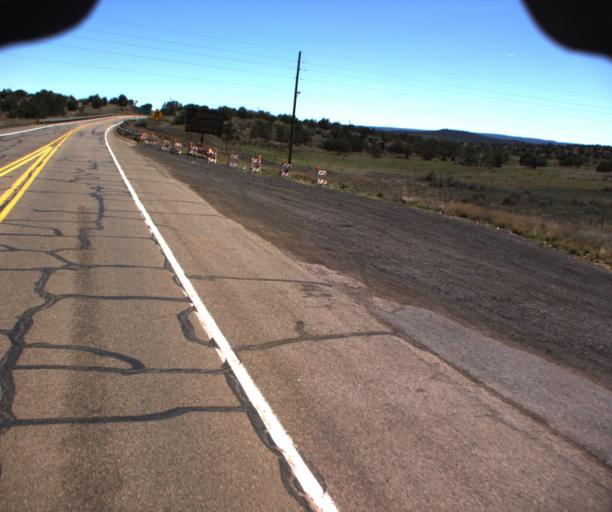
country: US
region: Arizona
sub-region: Coconino County
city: Williams
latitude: 35.2199
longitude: -112.4741
